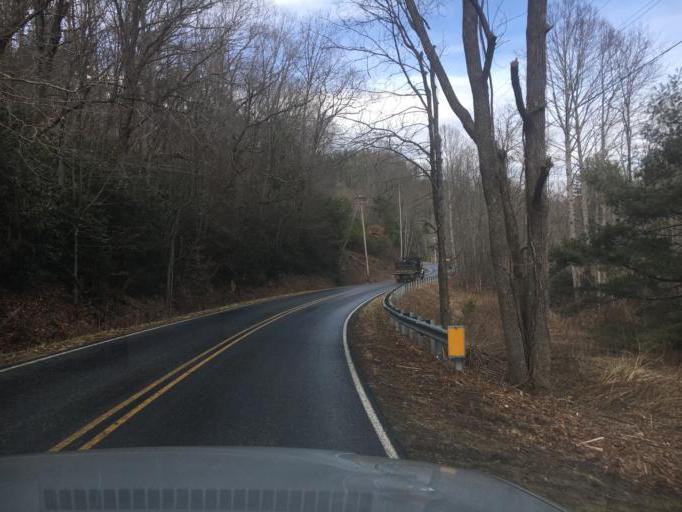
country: US
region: North Carolina
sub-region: Haywood County
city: Canton
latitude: 35.4057
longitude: -82.8133
